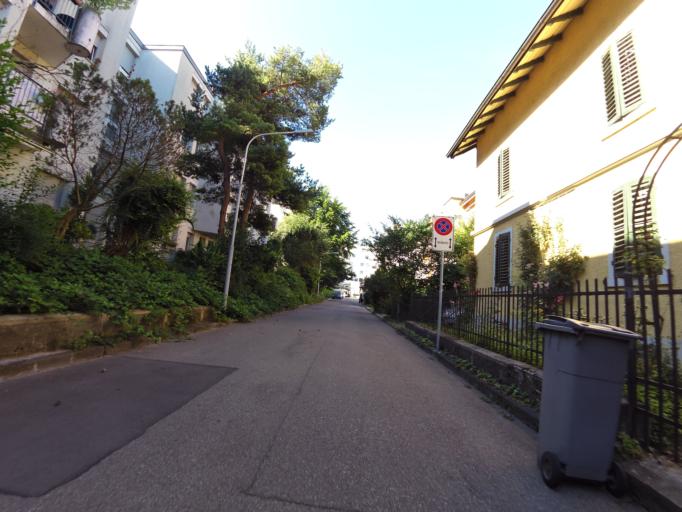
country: CH
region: Zurich
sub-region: Bezirk Zuerich
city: Zuerich (Kreis 9) / Altstetten
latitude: 47.3898
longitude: 8.4849
